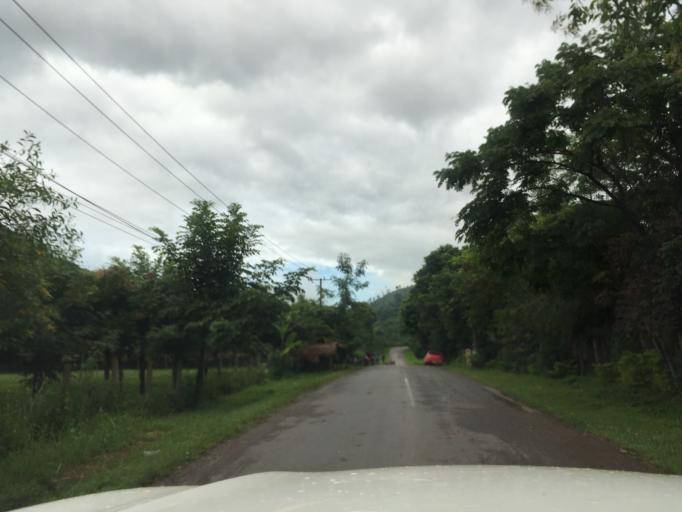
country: LA
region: Oudomxai
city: Muang La
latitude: 20.7902
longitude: 102.0808
